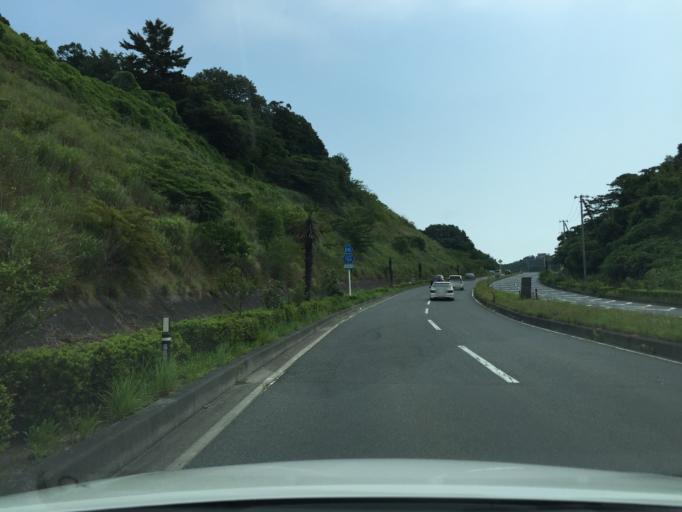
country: JP
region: Fukushima
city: Iwaki
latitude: 36.9730
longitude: 140.9059
